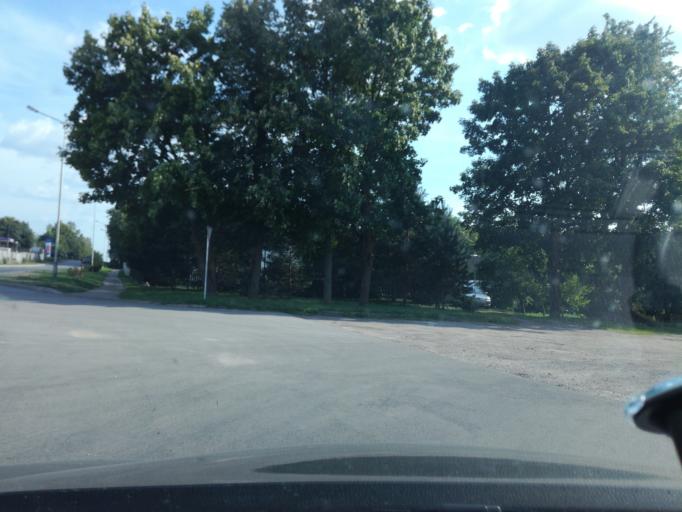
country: LT
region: Marijampoles apskritis
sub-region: Marijampole Municipality
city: Marijampole
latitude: 54.5355
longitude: 23.3519
